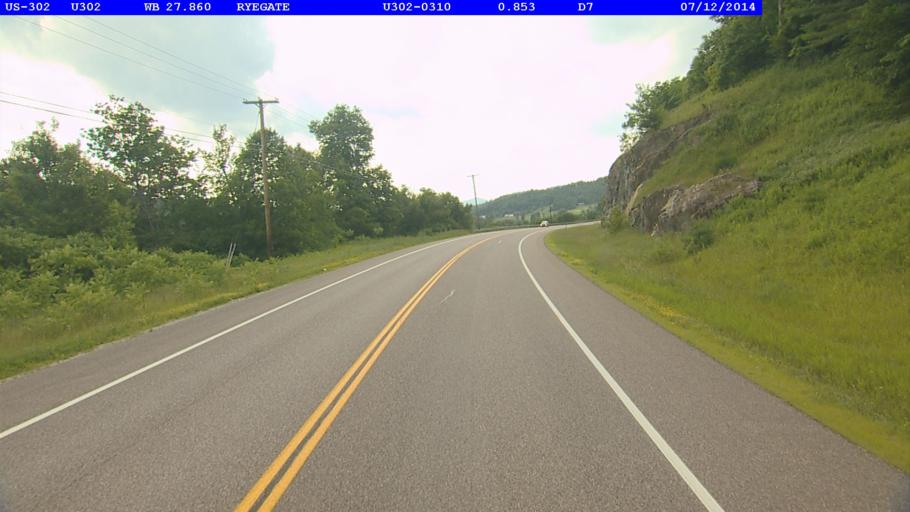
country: US
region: New Hampshire
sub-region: Grafton County
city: Woodsville
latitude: 44.1977
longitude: -72.1578
